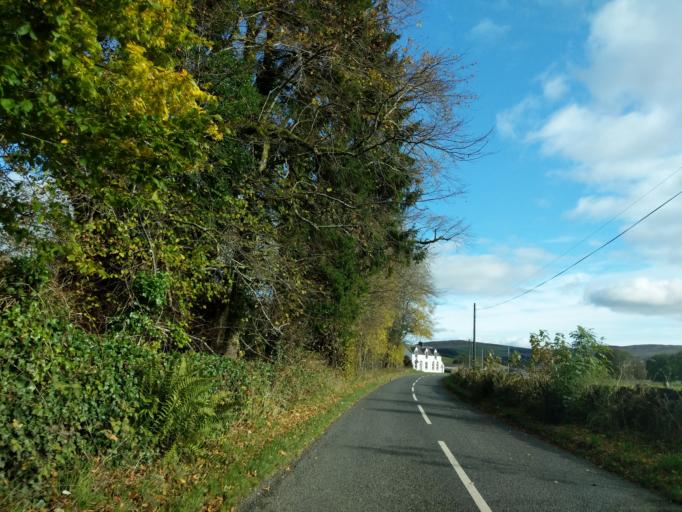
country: GB
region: Scotland
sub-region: Dumfries and Galloway
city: Sanquhar
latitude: 55.1605
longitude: -3.9927
